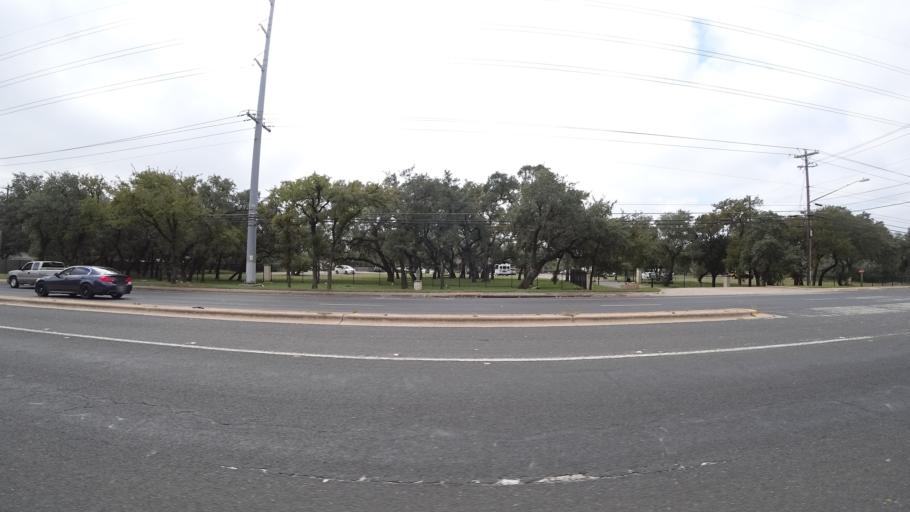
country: US
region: Texas
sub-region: Travis County
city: Shady Hollow
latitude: 30.1806
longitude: -97.8435
